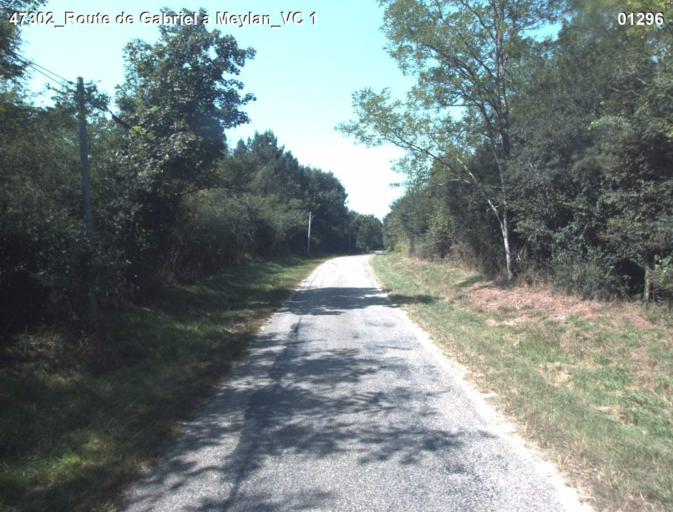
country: FR
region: Aquitaine
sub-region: Departement du Lot-et-Garonne
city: Mezin
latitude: 44.0632
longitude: 0.1427
